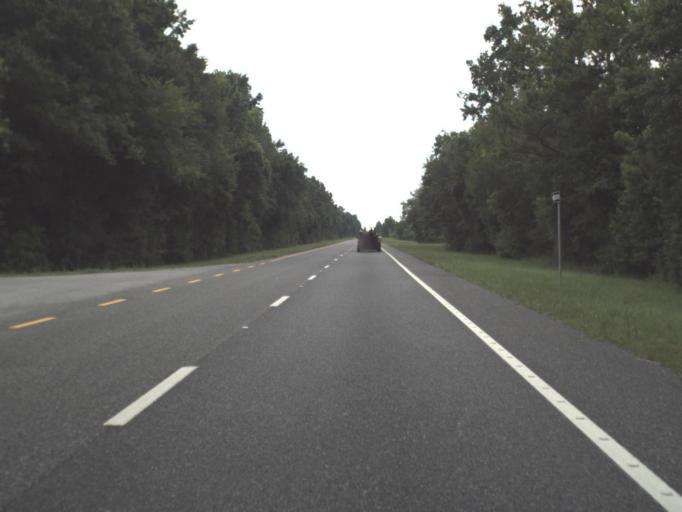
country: US
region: Florida
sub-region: Levy County
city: Williston Highlands
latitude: 29.2586
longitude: -82.7263
